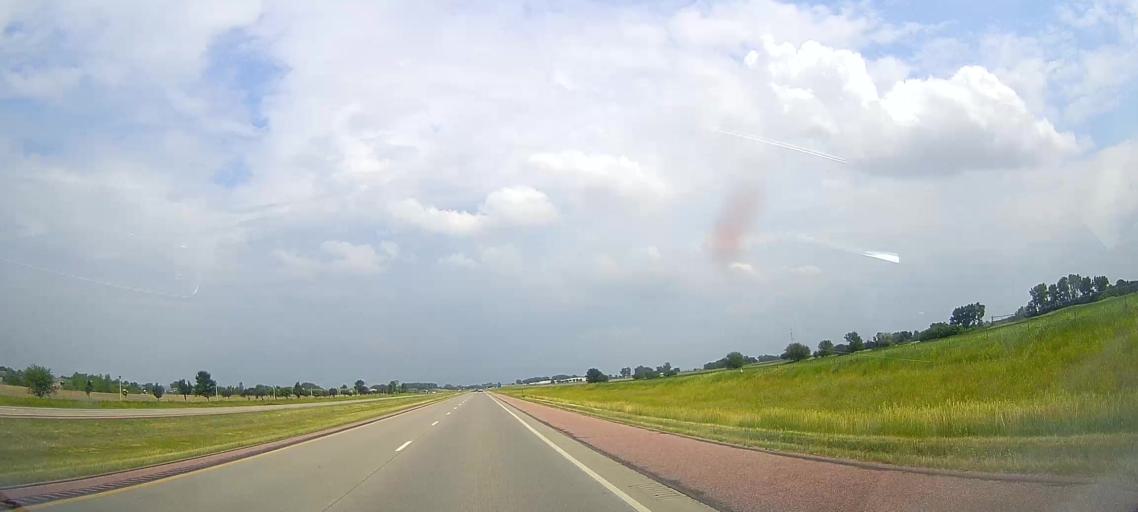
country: US
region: South Dakota
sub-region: Union County
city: Elk Point
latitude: 42.6730
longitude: -96.6802
